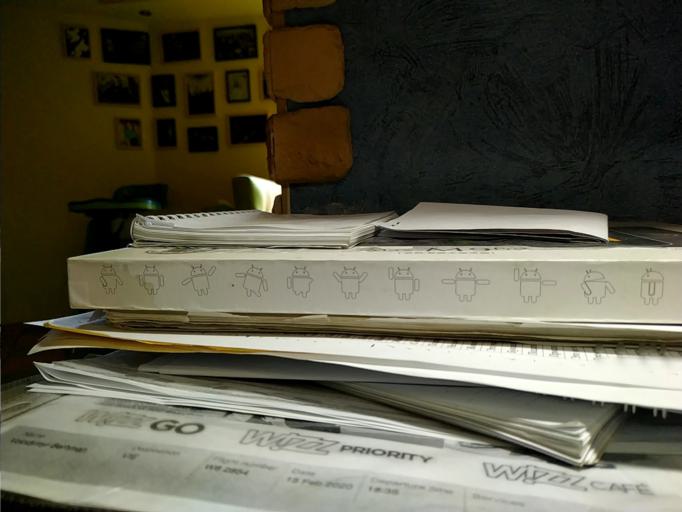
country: RU
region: Pskov
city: Plyussa
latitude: 58.3840
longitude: 29.7163
